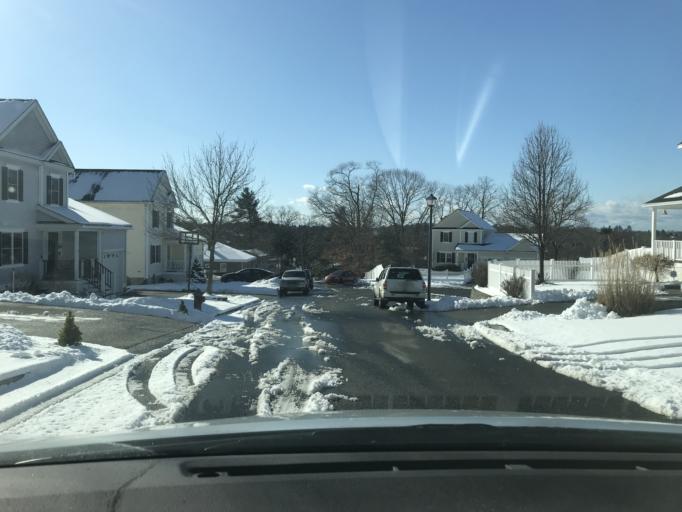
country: US
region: Massachusetts
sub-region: Essex County
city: Saugus
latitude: 42.4764
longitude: -71.0073
